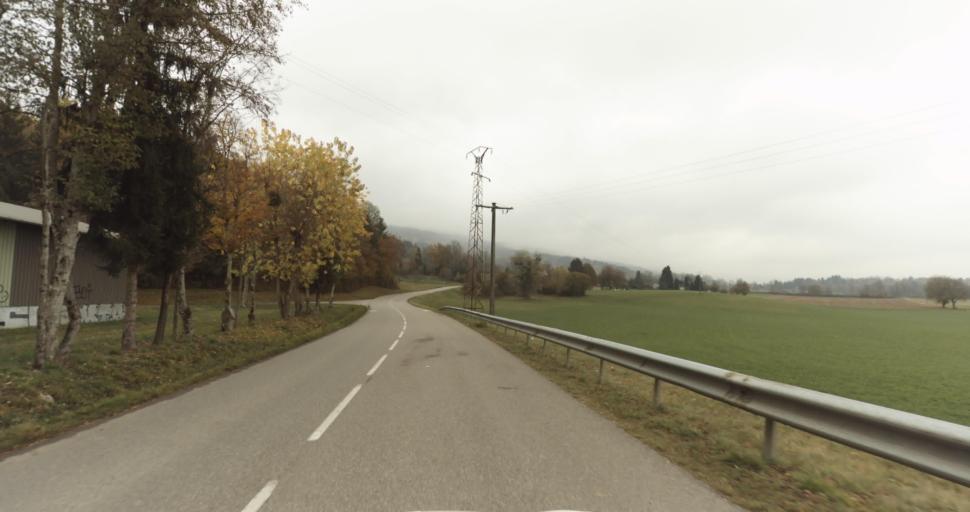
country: FR
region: Rhone-Alpes
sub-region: Departement de la Haute-Savoie
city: Viuz-la-Chiesaz
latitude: 45.8179
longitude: 6.0590
